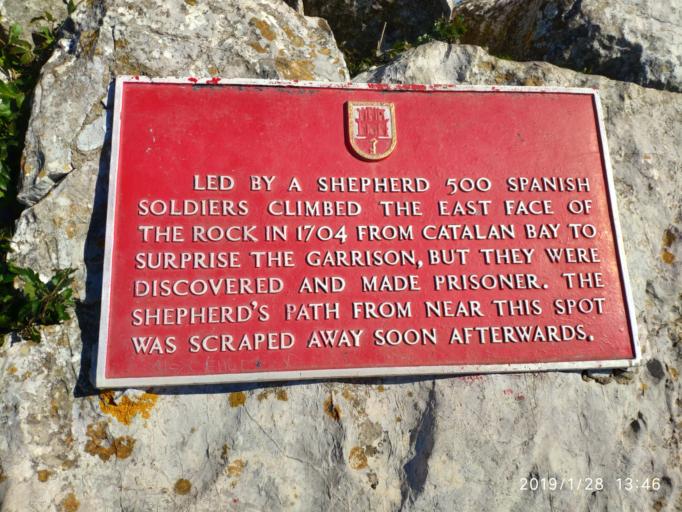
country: GI
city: Gibraltar
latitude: 36.1311
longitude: -5.3455
